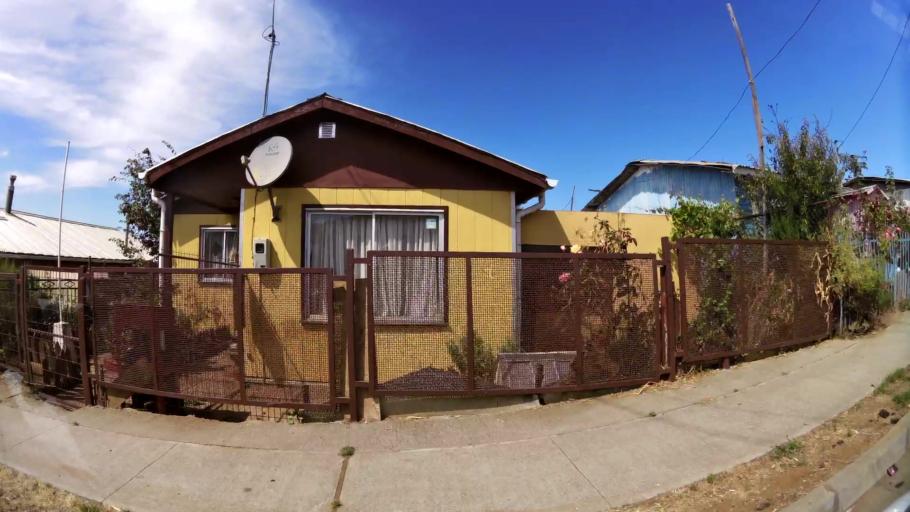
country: CL
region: Biobio
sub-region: Provincia de Concepcion
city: Talcahuano
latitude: -36.7089
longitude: -73.1214
